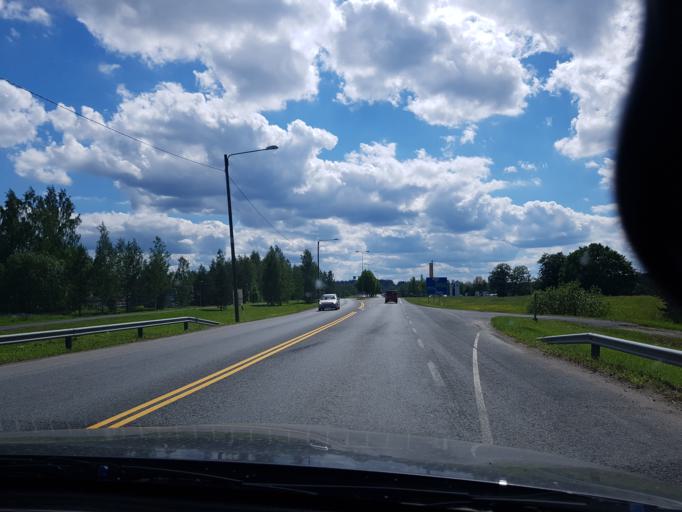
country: FI
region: Haeme
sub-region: Haemeenlinna
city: Haemeenlinna
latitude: 61.0182
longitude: 24.4206
